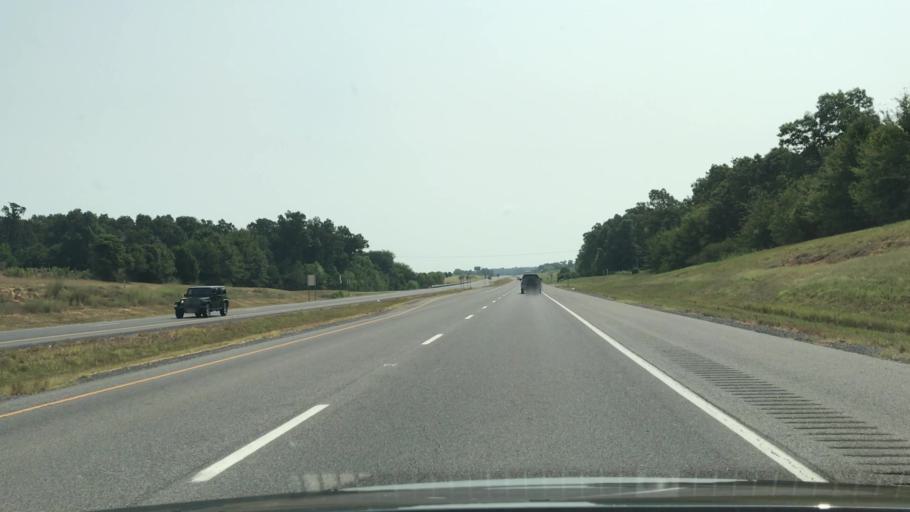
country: US
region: Kentucky
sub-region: Calloway County
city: Murray
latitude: 36.6504
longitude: -88.2651
